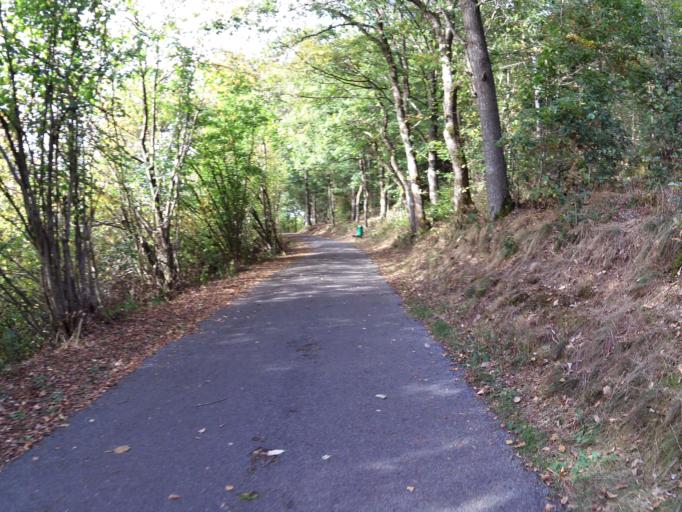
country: BE
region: Wallonia
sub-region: Province de Liege
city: Saint-Vith
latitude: 50.2689
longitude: 6.1380
